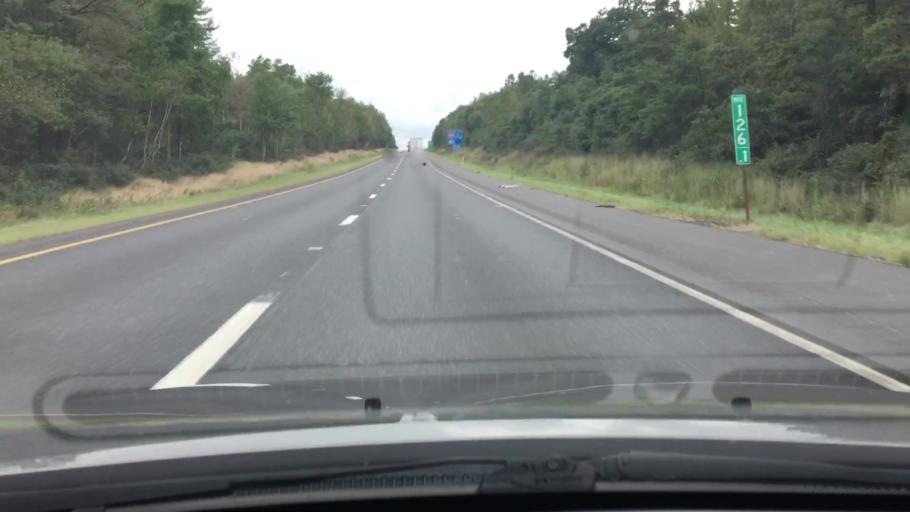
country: US
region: Pennsylvania
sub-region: Schuylkill County
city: Shenandoah
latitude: 40.7787
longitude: -76.1855
